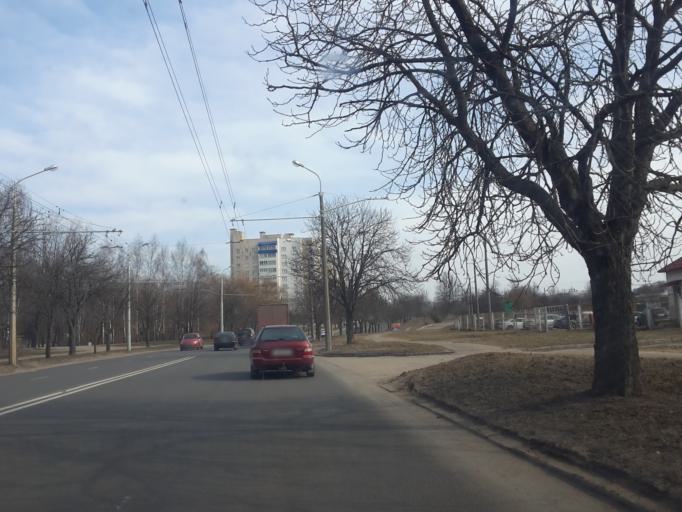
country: BY
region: Minsk
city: Minsk
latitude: 53.8987
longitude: 27.5088
